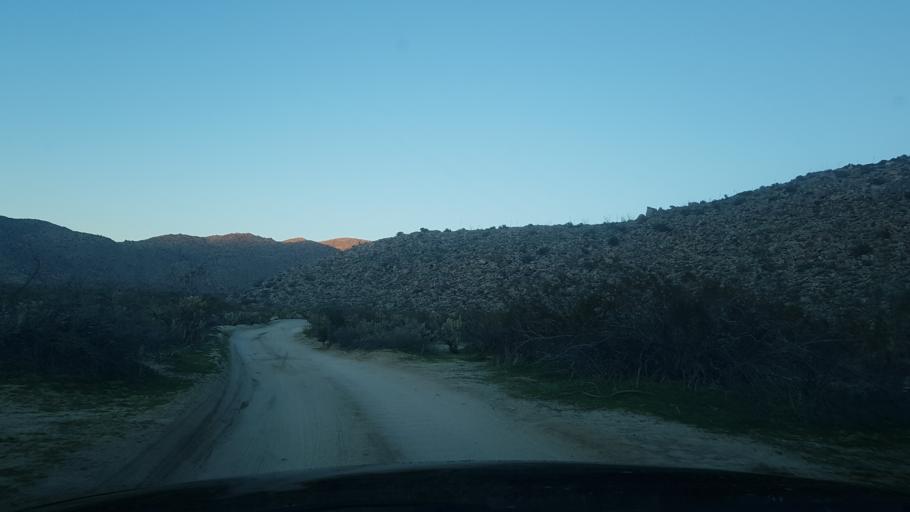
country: US
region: California
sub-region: San Diego County
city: Julian
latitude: 33.0115
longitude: -116.3761
